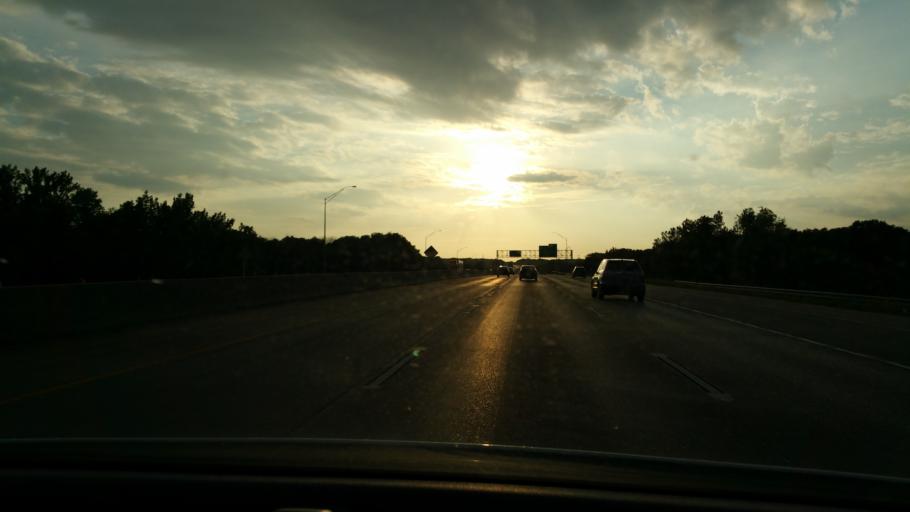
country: US
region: Iowa
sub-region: Polk County
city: Johnston
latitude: 41.6517
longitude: -93.6858
